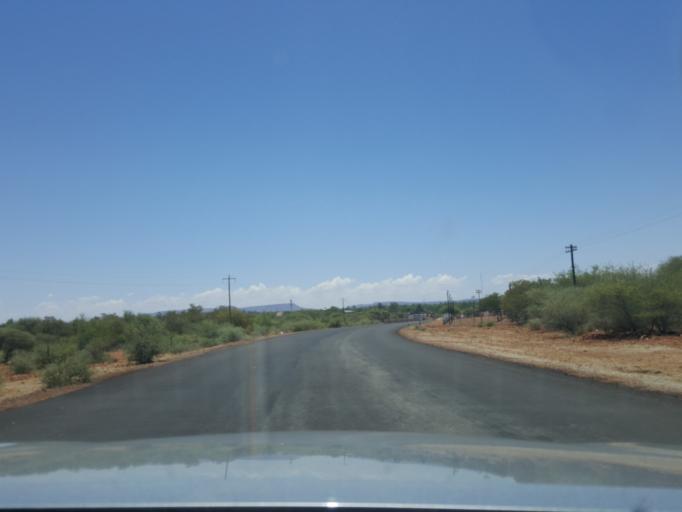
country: BW
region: South East
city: Ramotswa
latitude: -24.8754
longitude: 25.8899
